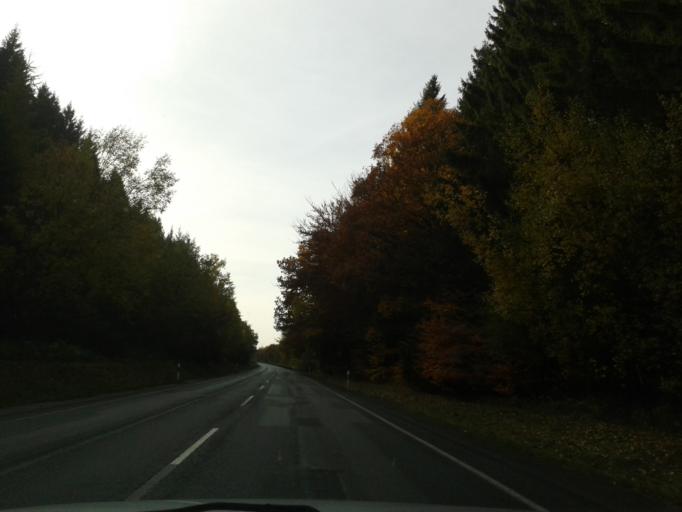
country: DE
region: North Rhine-Westphalia
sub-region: Regierungsbezirk Arnsberg
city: Ruthen
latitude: 51.4255
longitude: 8.4349
